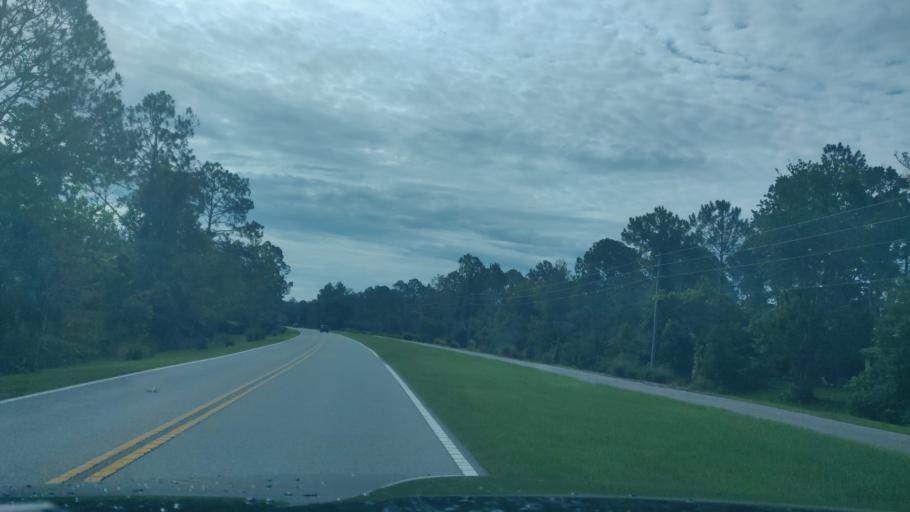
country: US
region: Florida
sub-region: Flagler County
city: Bunnell
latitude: 29.5176
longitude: -81.2361
